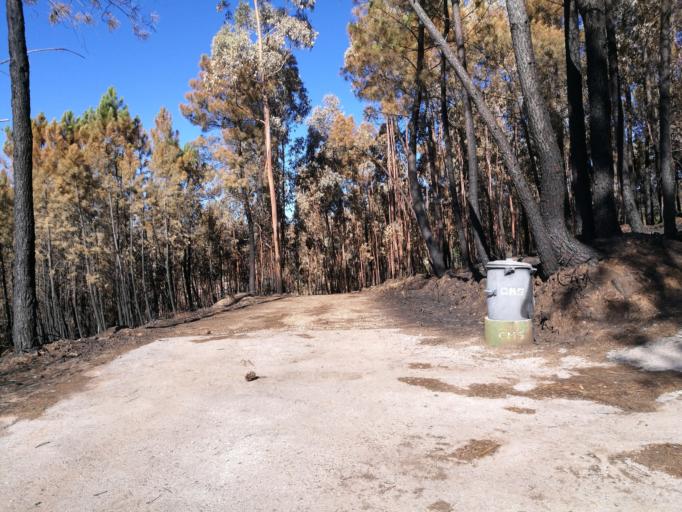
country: PT
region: Leiria
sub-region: Pedrogao Grande
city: Pedrogao Grande
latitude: 39.9134
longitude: -8.0660
